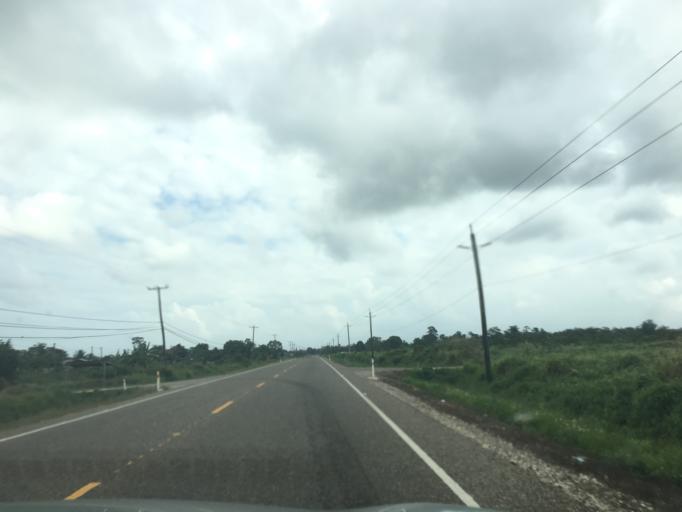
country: BZ
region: Stann Creek
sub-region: Dangriga
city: Dangriga
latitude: 16.9967
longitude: -88.3418
